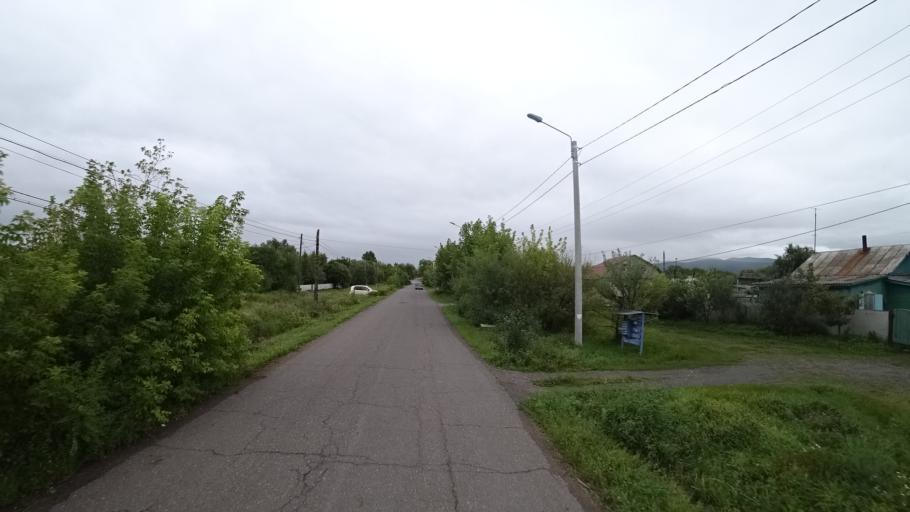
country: RU
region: Primorskiy
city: Chernigovka
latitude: 44.3369
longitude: 132.5854
